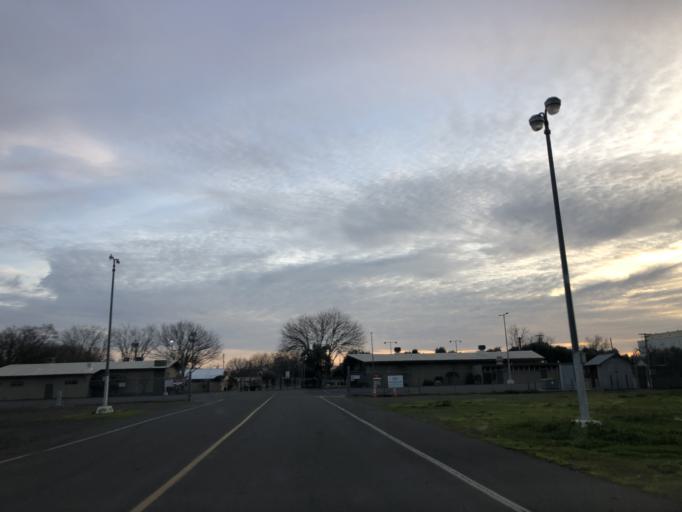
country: US
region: California
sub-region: Yolo County
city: Woodland
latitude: 38.6673
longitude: -121.7636
